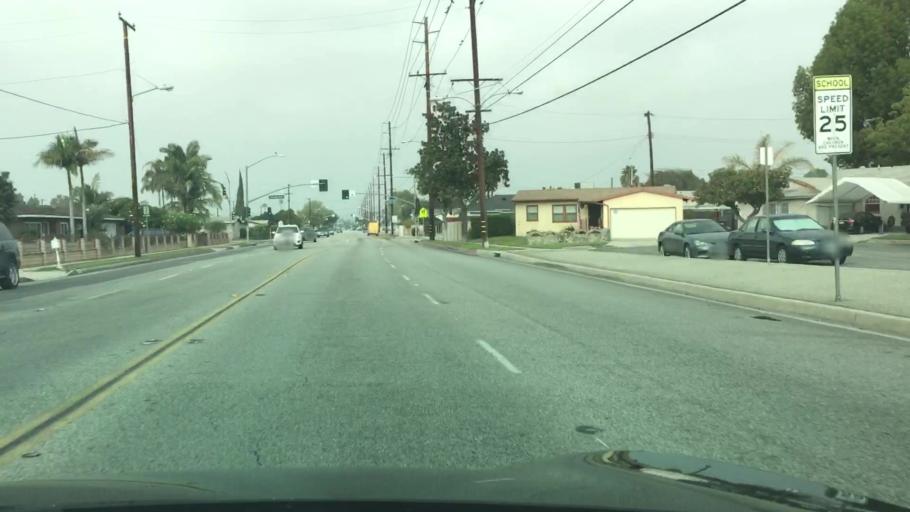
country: US
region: California
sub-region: Los Angeles County
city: West Puente Valley
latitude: 34.0435
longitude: -117.9718
